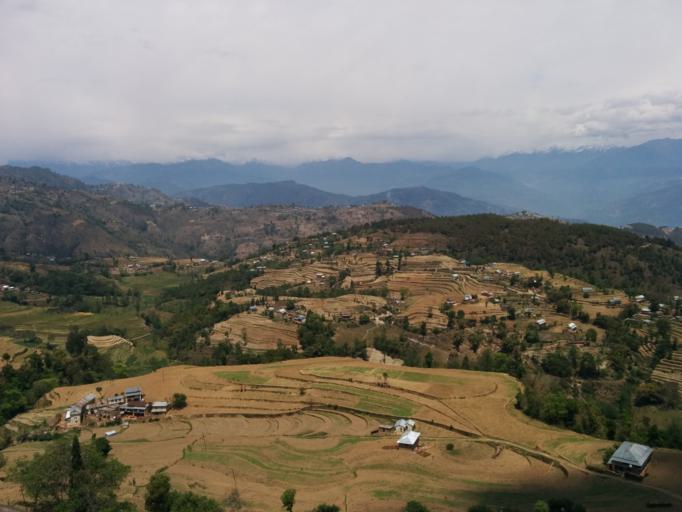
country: NP
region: Central Region
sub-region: Bagmati Zone
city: Nagarkot
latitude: 27.7338
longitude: 85.5104
